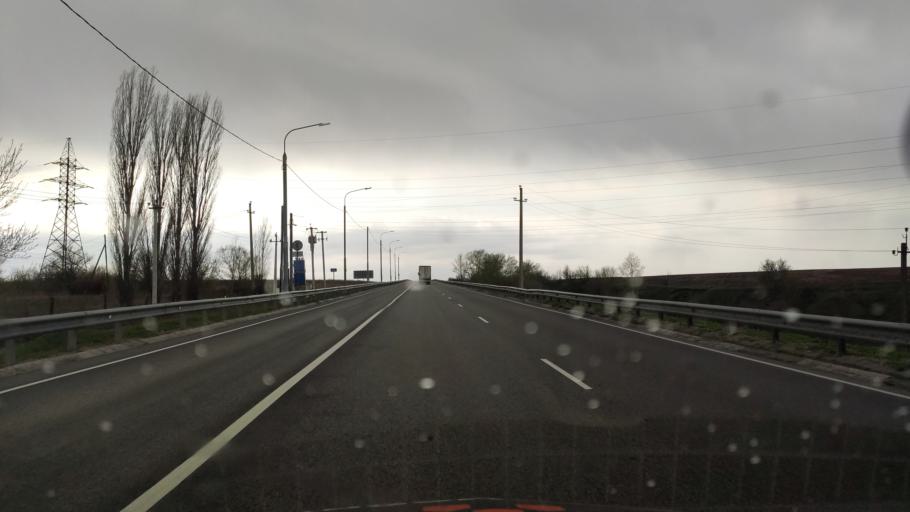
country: RU
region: Voronezj
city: Nizhnedevitsk
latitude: 51.5648
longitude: 38.3626
